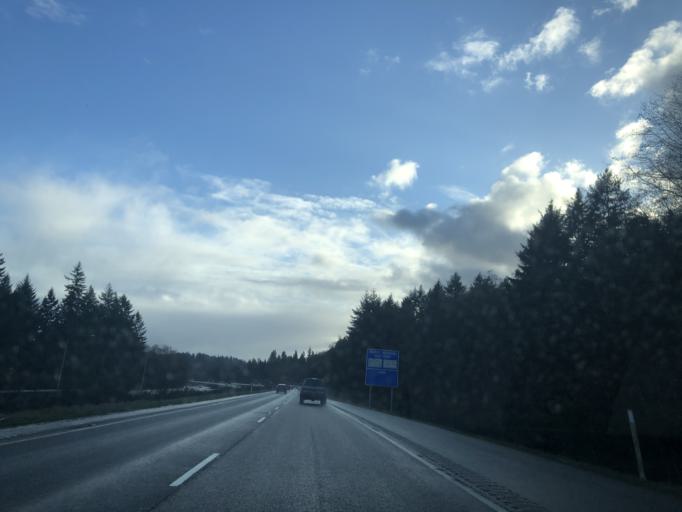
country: US
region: Washington
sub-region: Kitsap County
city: Chico
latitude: 47.6099
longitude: -122.7129
